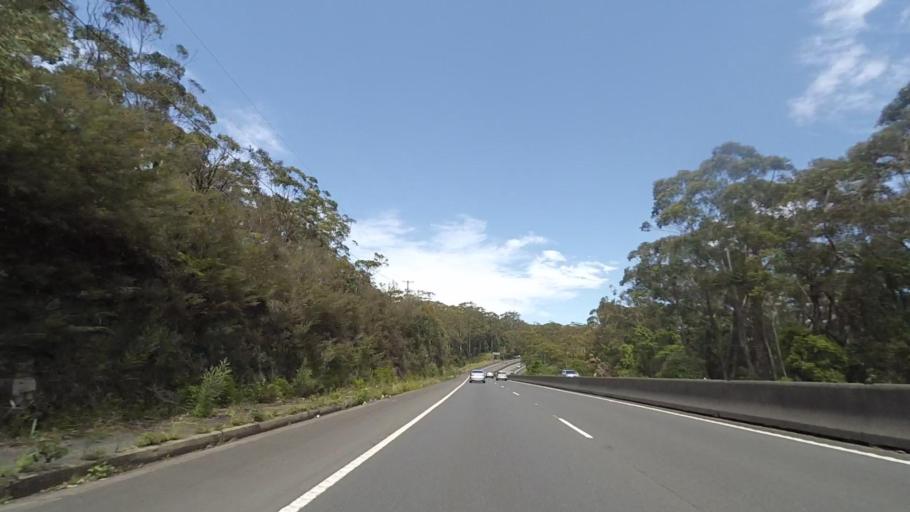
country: AU
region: New South Wales
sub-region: Wollongong
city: Bulli
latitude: -34.3195
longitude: 150.8894
